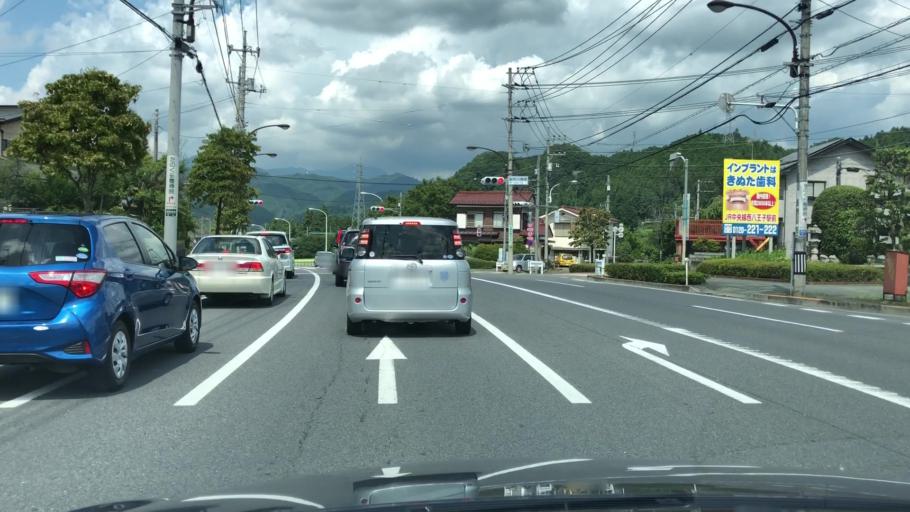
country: JP
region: Tokyo
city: Itsukaichi
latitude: 35.7282
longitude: 139.2444
